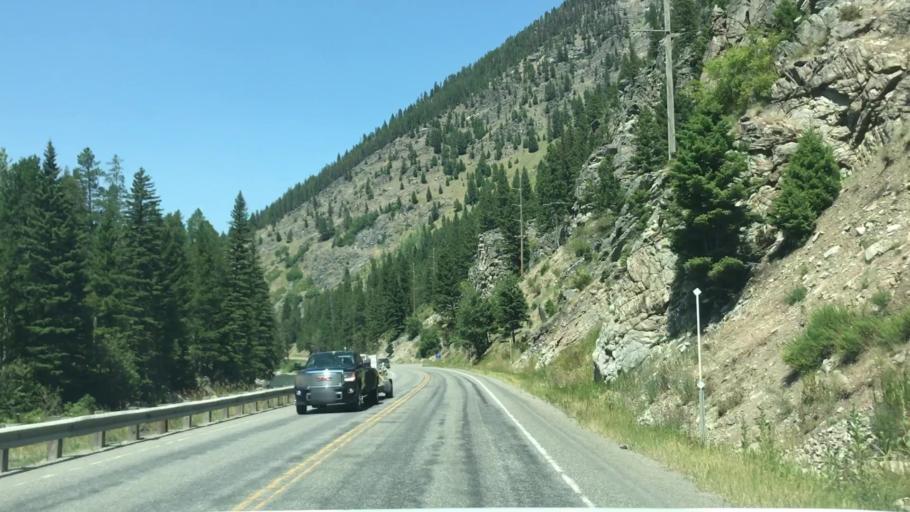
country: US
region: Montana
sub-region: Gallatin County
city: Big Sky
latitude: 45.4022
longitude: -111.2181
